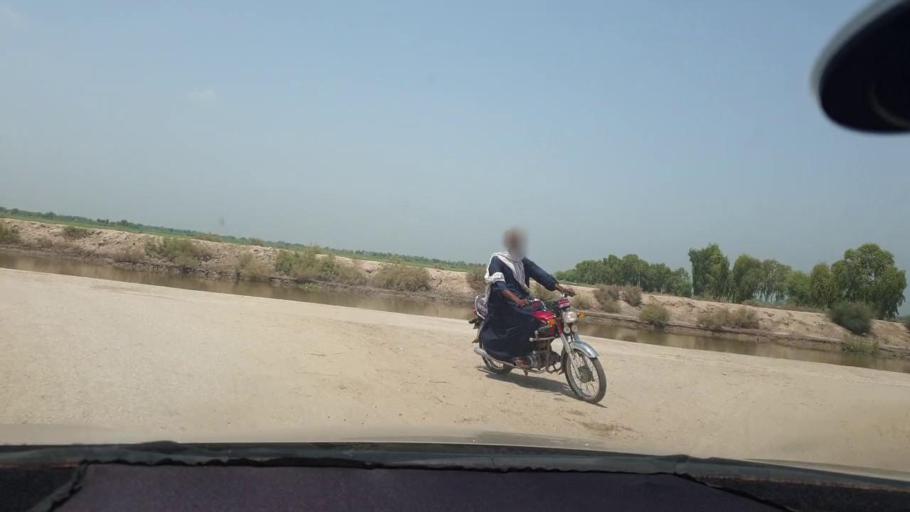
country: PK
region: Sindh
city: Kambar
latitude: 27.6770
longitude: 67.9094
